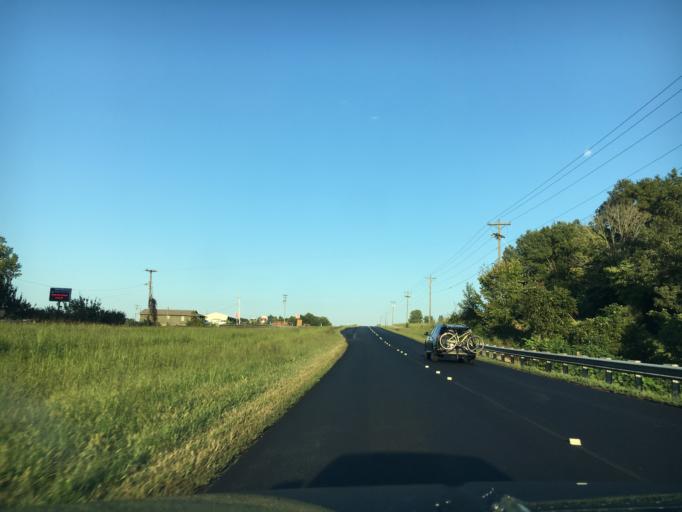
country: US
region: Virginia
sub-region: City of Danville
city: Danville
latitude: 36.5806
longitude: -79.2481
